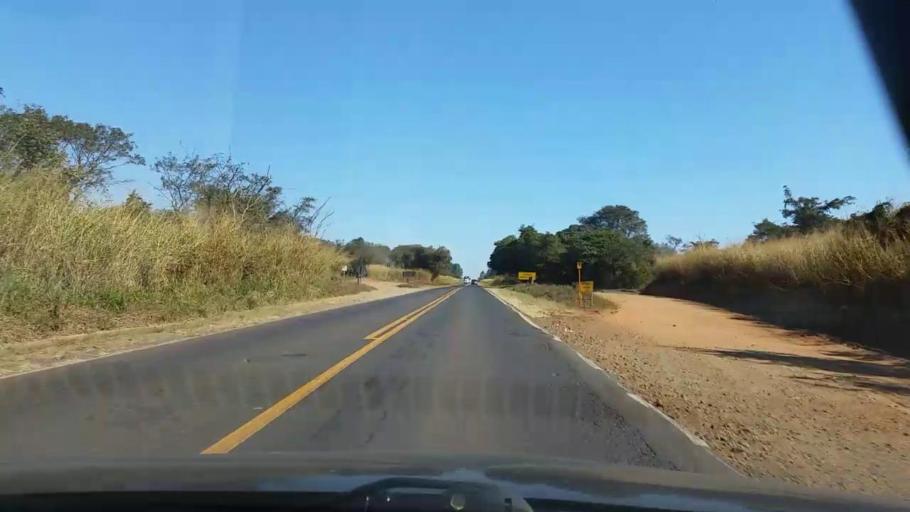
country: BR
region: Sao Paulo
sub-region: Avare
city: Avare
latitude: -22.9143
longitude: -48.7773
